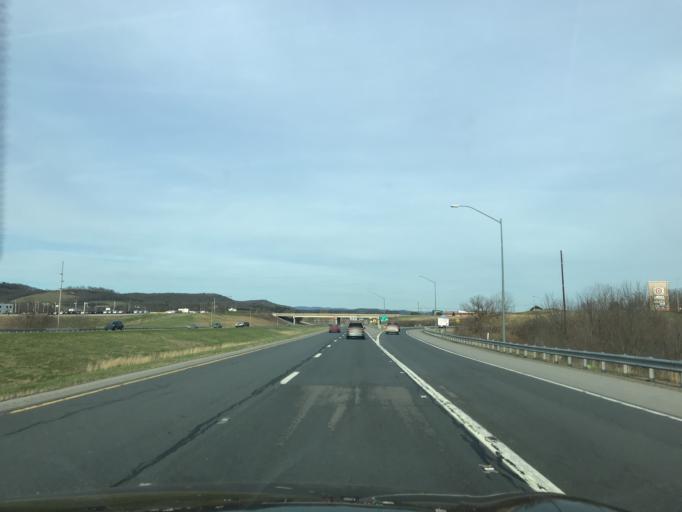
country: US
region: Pennsylvania
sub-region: Lycoming County
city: Muncy
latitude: 41.2456
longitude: -76.8386
